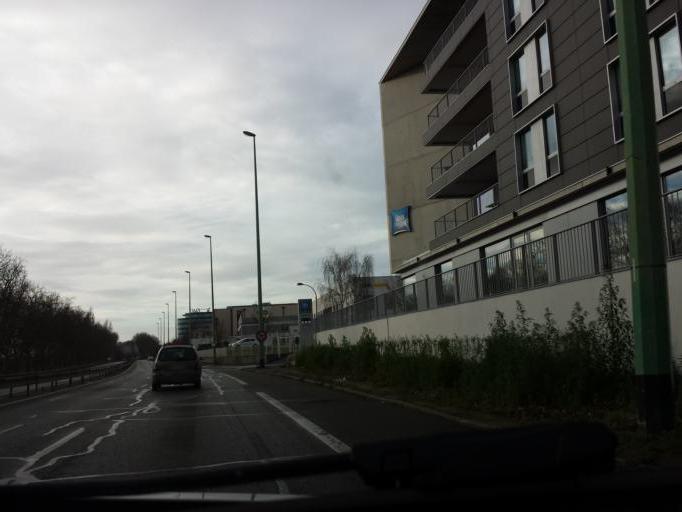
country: FR
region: Ile-de-France
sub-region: Departement du Val-d'Oise
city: Bezons
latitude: 48.9273
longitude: 2.2284
